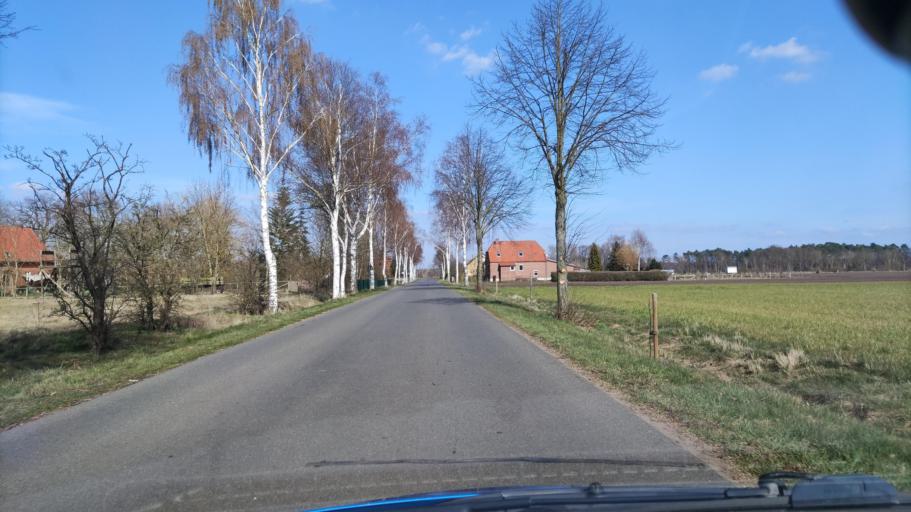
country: DE
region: Lower Saxony
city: Klein Gusborn
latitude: 53.0538
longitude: 11.2263
